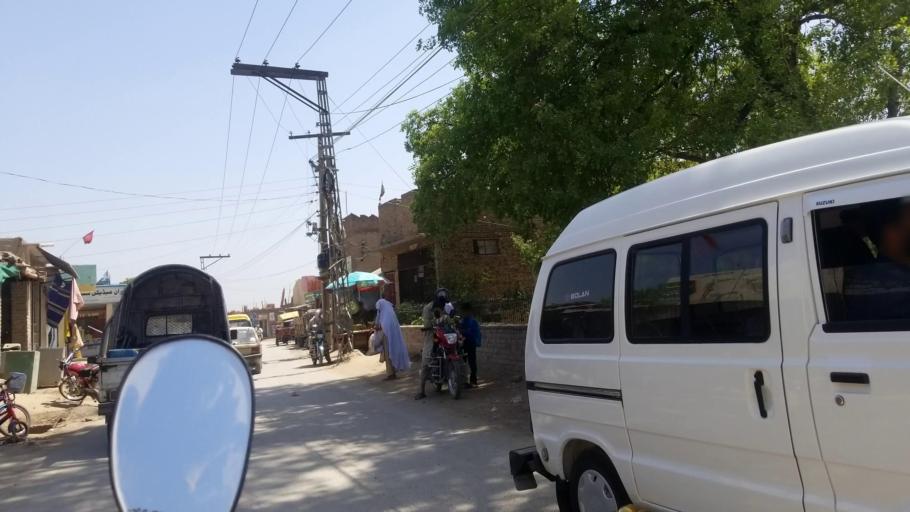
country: PK
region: Khyber Pakhtunkhwa
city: Peshawar
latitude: 34.0303
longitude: 71.4854
